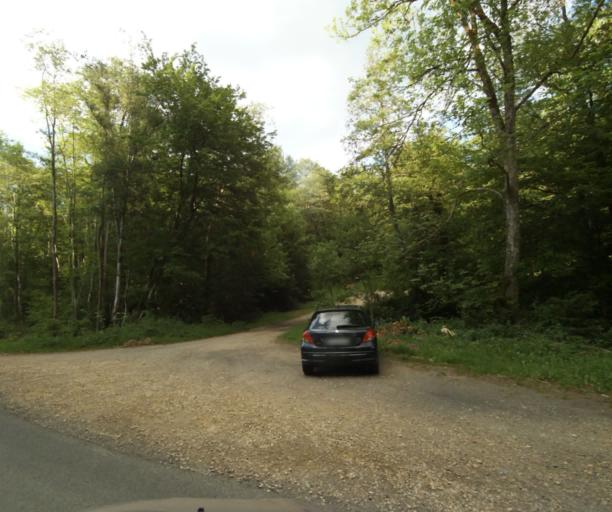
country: FR
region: Champagne-Ardenne
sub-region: Departement des Ardennes
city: Nouzonville
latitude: 49.8228
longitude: 4.7129
